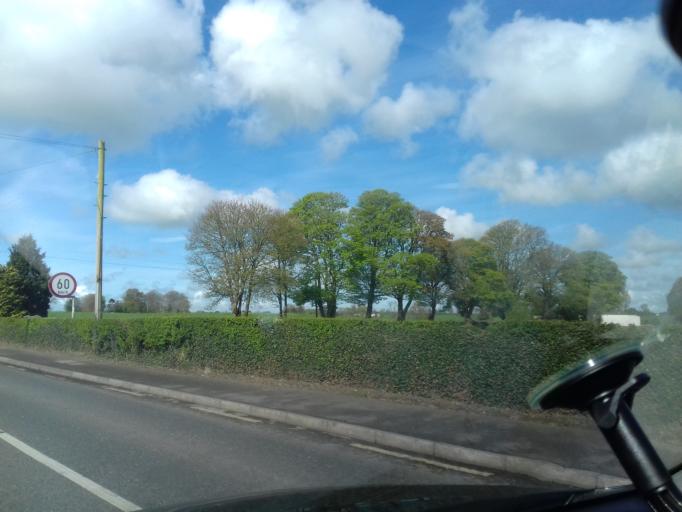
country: IE
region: Leinster
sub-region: An Mhi
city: Kells
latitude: 53.7206
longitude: -6.8841
